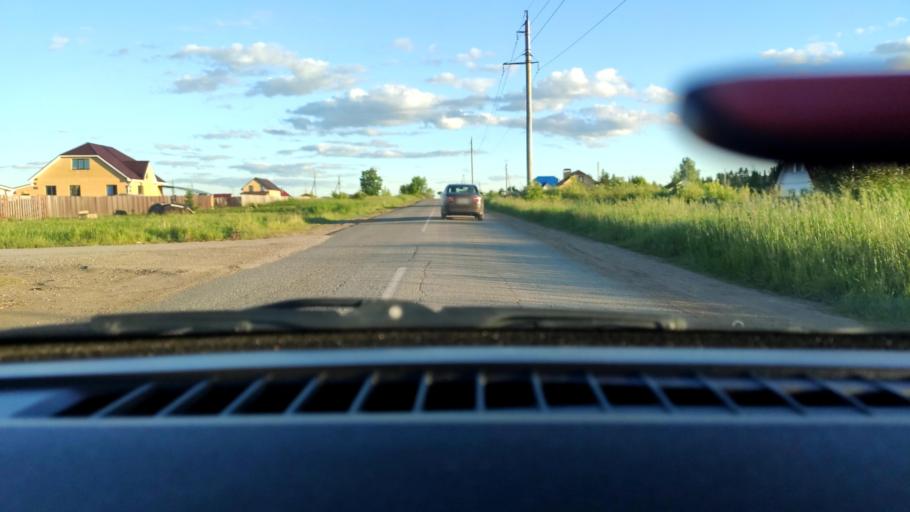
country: RU
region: Perm
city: Kultayevo
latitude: 57.9347
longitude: 55.8645
